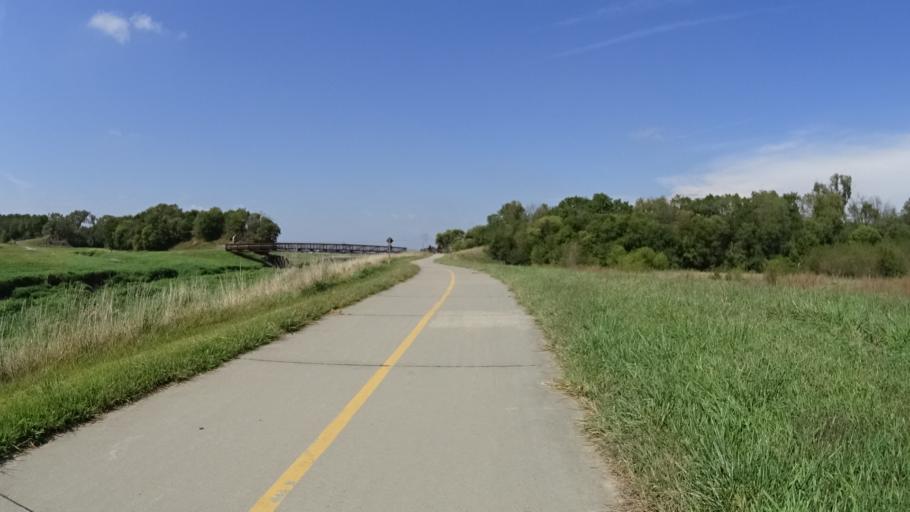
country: US
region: Nebraska
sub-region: Sarpy County
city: Offutt Air Force Base
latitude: 41.1497
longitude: -95.9676
